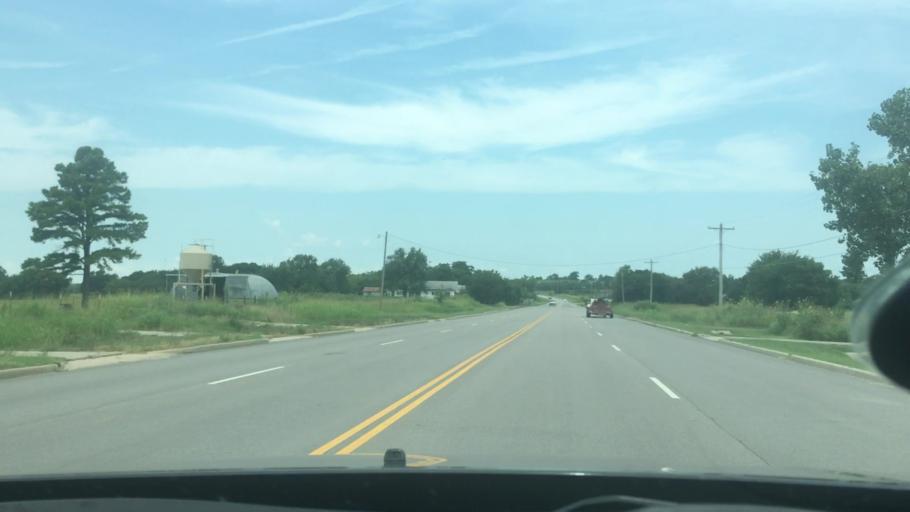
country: US
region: Oklahoma
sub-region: Seminole County
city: Seminole
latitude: 35.2657
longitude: -96.7165
